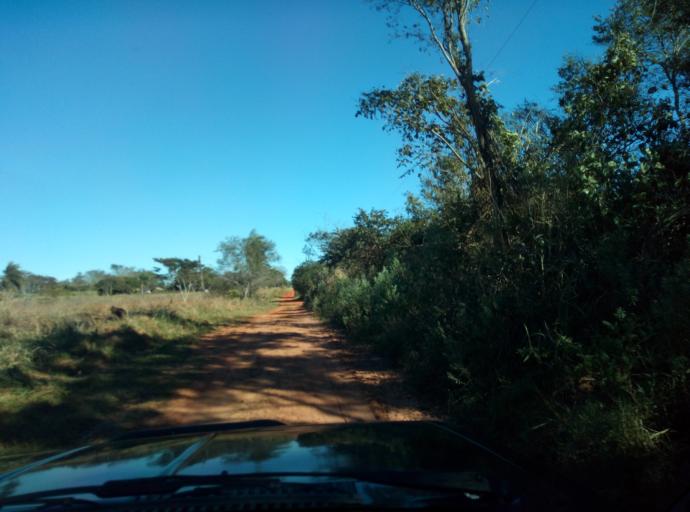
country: PY
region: Caaguazu
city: Doctor Cecilio Baez
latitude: -25.1790
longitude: -56.2391
